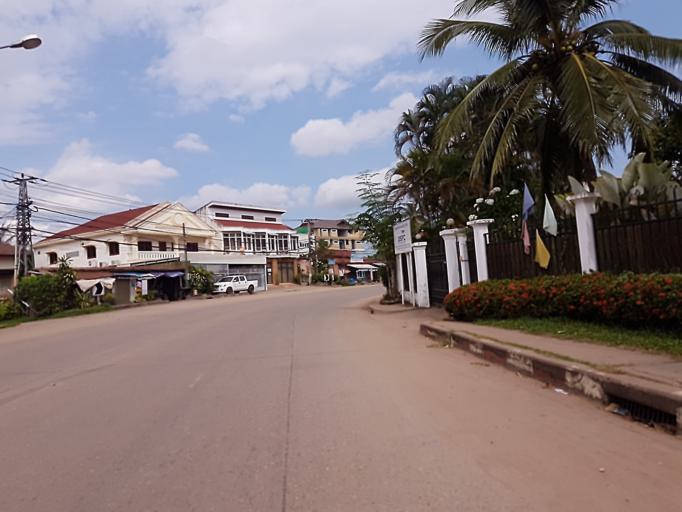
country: LA
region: Vientiane
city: Vientiane
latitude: 17.9389
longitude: 102.6200
